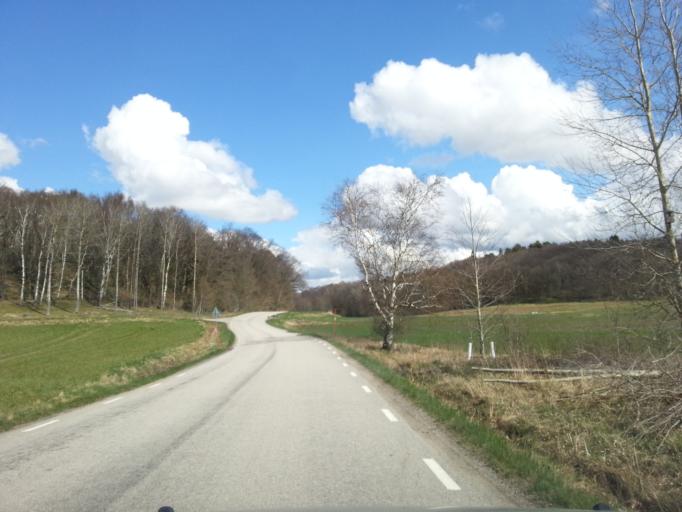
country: SE
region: Vaestra Goetaland
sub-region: Kungalvs Kommun
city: Kode
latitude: 57.8394
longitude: 11.8731
